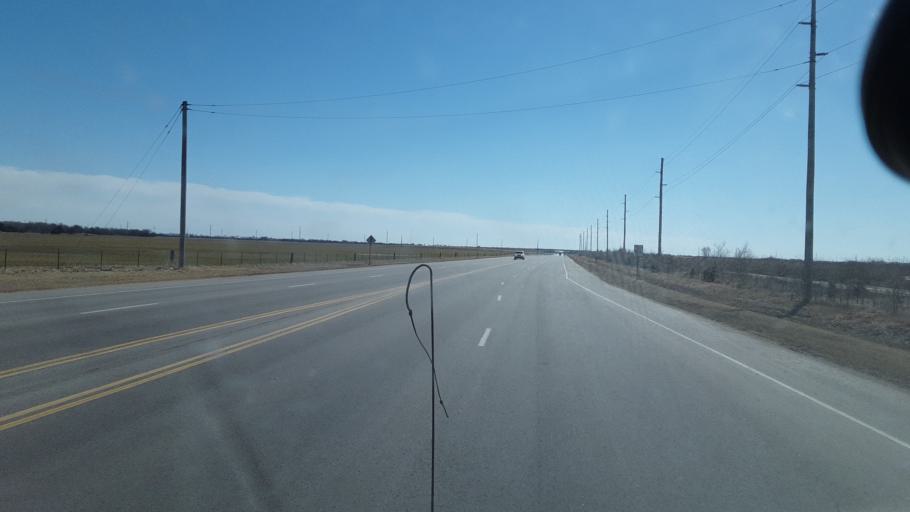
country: US
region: Kansas
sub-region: Reno County
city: Hutchinson
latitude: 38.0417
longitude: -97.8669
